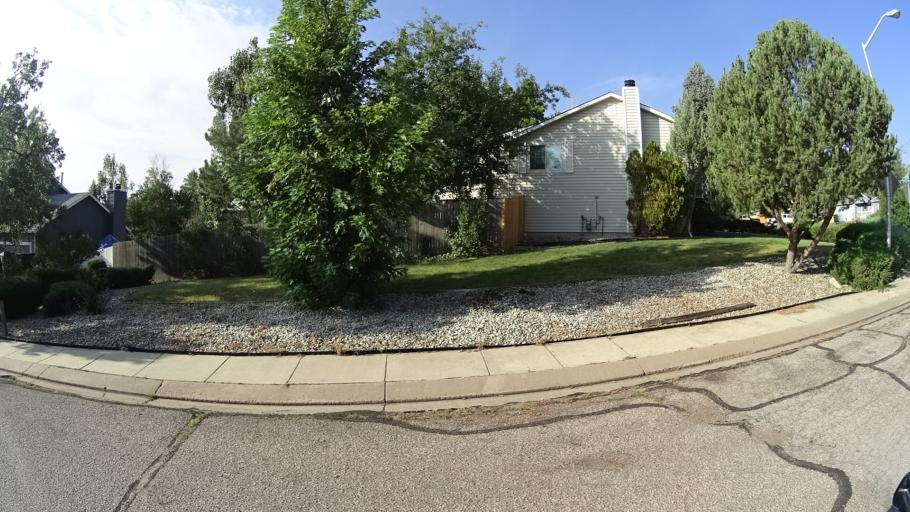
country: US
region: Colorado
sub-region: El Paso County
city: Colorado Springs
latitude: 38.8836
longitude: -104.7925
